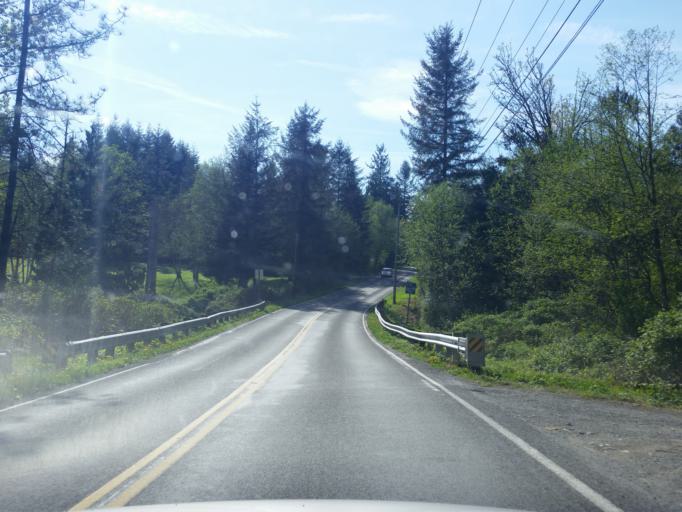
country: US
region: Washington
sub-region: Snohomish County
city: Three Lakes
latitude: 47.9634
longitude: -122.0195
